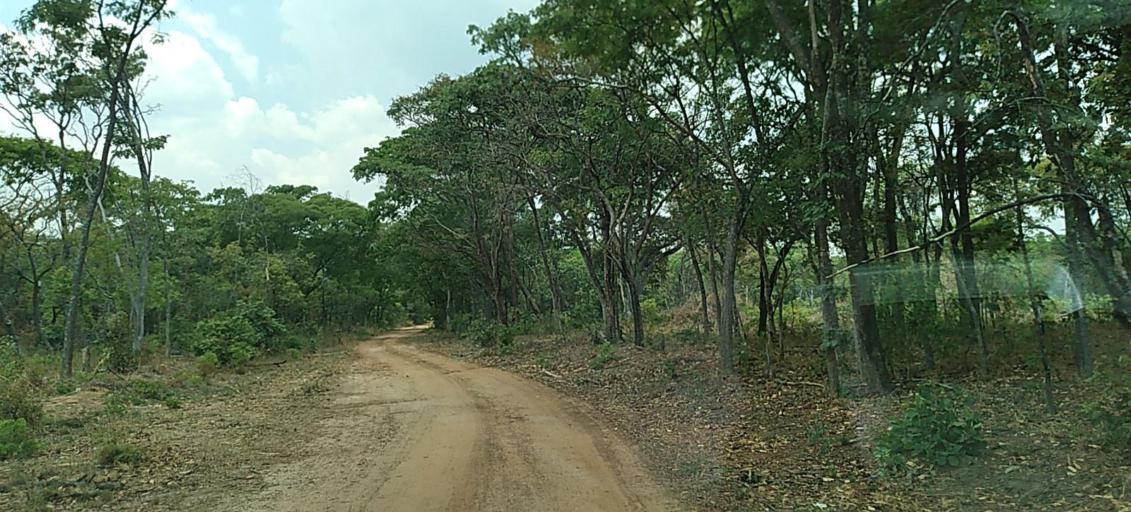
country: ZM
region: Copperbelt
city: Chingola
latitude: -12.7712
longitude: 27.6871
